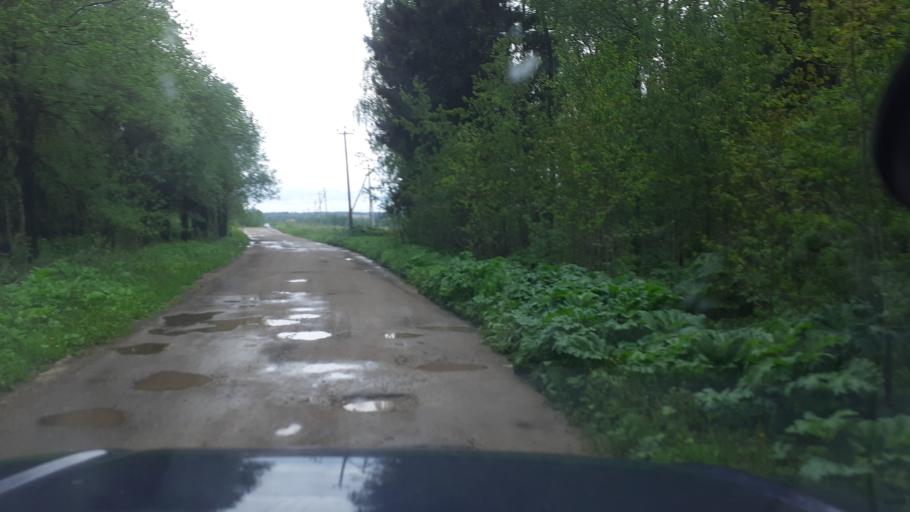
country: RU
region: Moskovskaya
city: Sychevo
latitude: 55.9671
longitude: 36.2436
